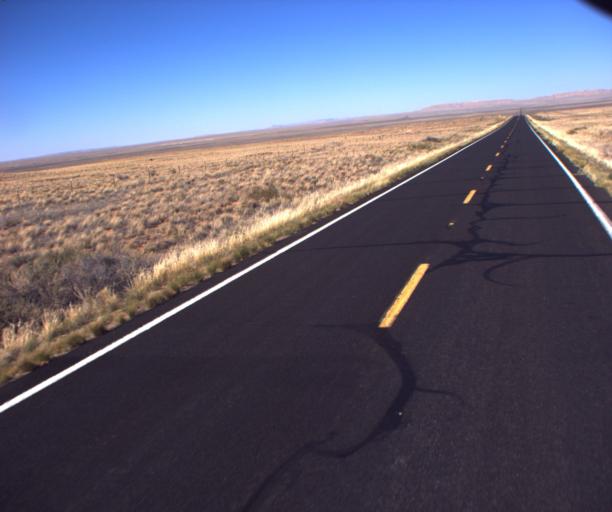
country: US
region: Arizona
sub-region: Navajo County
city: First Mesa
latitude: 35.6570
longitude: -110.4916
